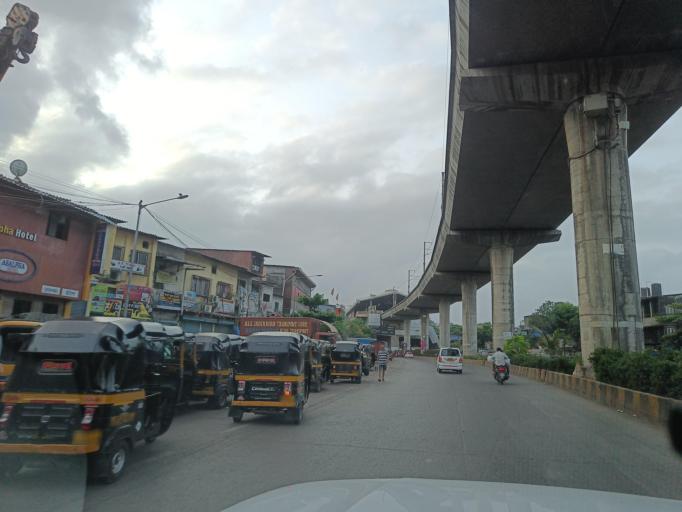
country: IN
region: Maharashtra
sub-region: Mumbai Suburban
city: Powai
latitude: 19.0979
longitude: 72.8931
